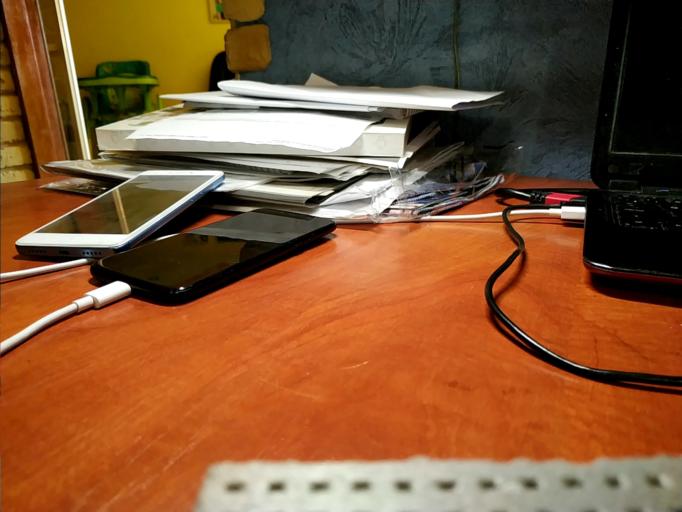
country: RU
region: Tverskaya
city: Kalashnikovo
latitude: 57.4112
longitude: 35.1651
